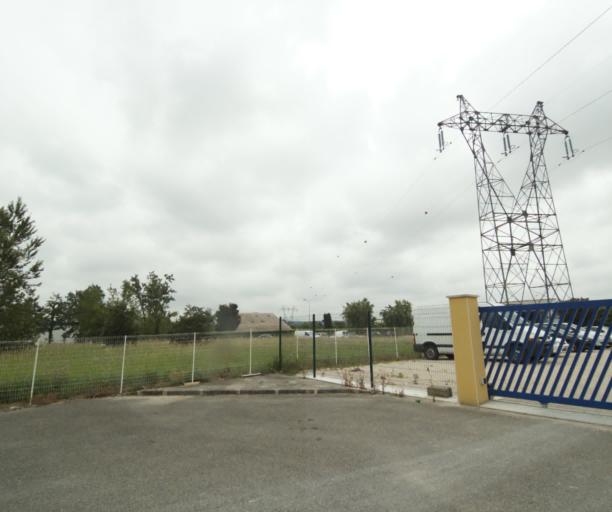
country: FR
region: Midi-Pyrenees
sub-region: Departement du Tarn-et-Garonne
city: Bressols
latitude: 43.9850
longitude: 1.3274
